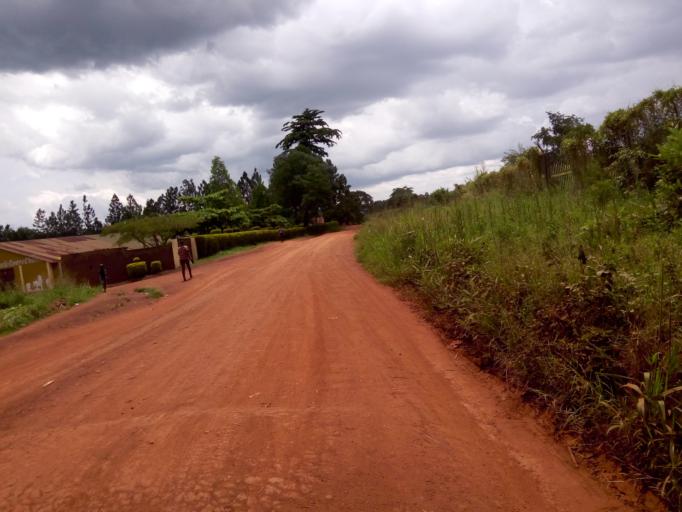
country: UG
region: Western Region
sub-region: Masindi District
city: Masindi
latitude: 1.6822
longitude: 31.7148
